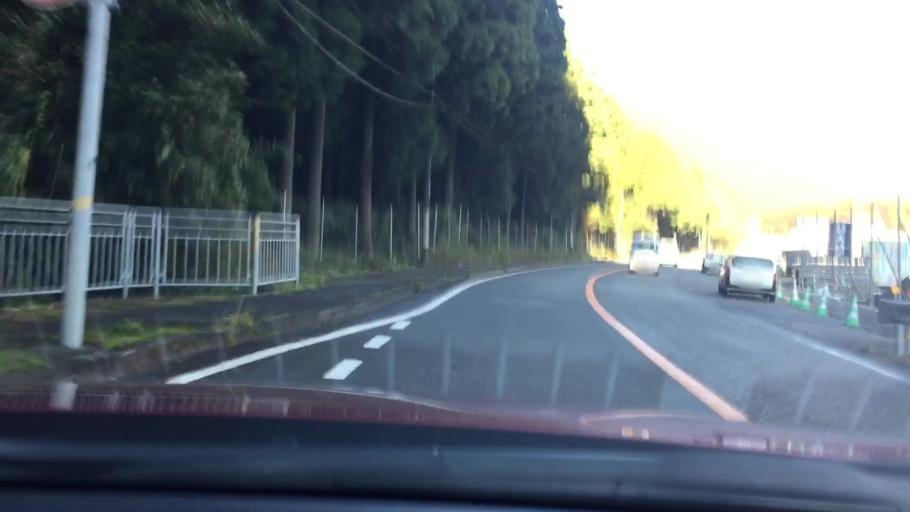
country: JP
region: Hyogo
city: Yamazakicho-nakabirose
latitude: 35.1295
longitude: 134.5643
